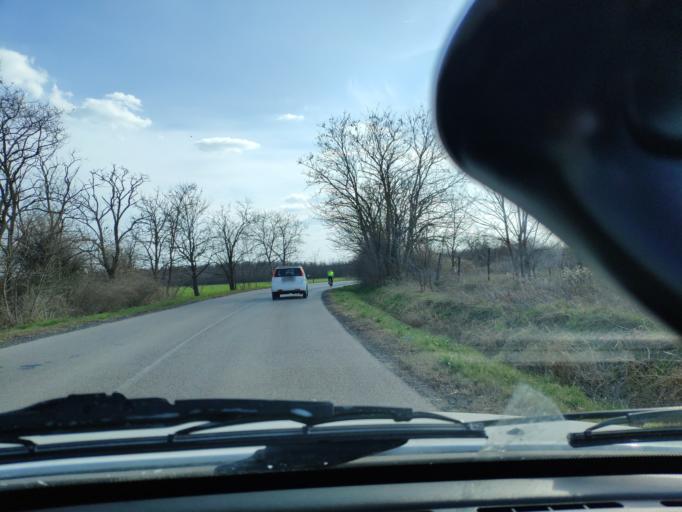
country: HU
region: Pest
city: Rackeve
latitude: 47.1433
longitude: 18.9119
